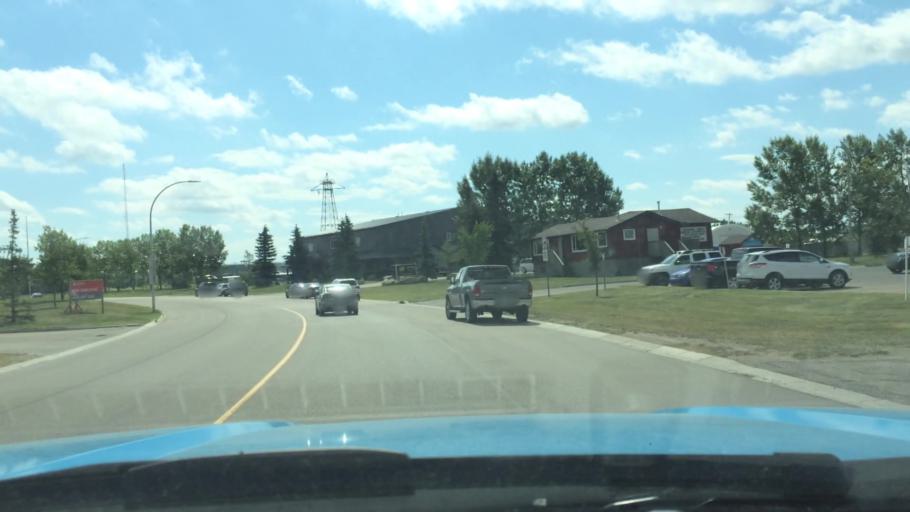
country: CA
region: Alberta
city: Airdrie
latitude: 51.2893
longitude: -113.9911
